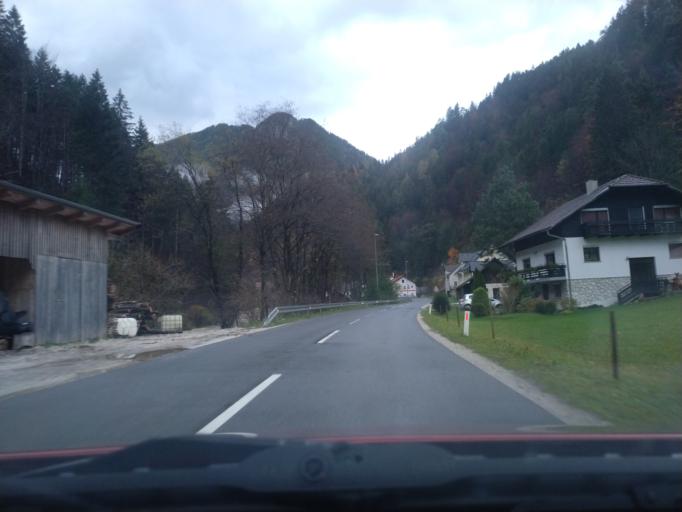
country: SI
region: Solcava
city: Solcava
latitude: 46.4174
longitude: 14.6981
